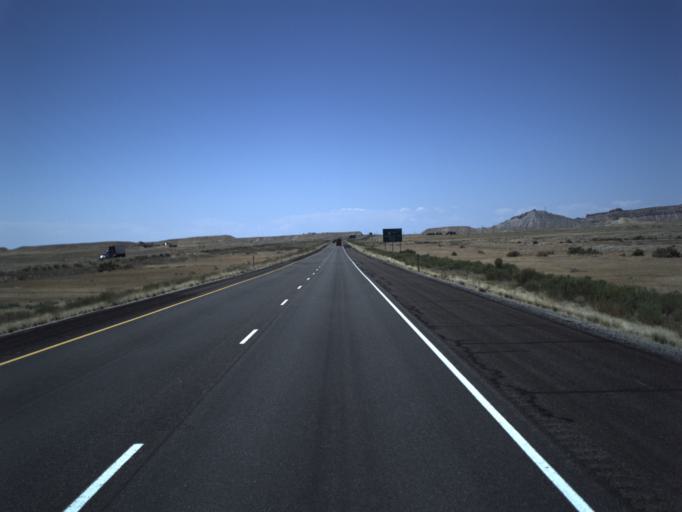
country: US
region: Utah
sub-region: Grand County
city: Moab
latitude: 38.9478
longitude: -109.7886
